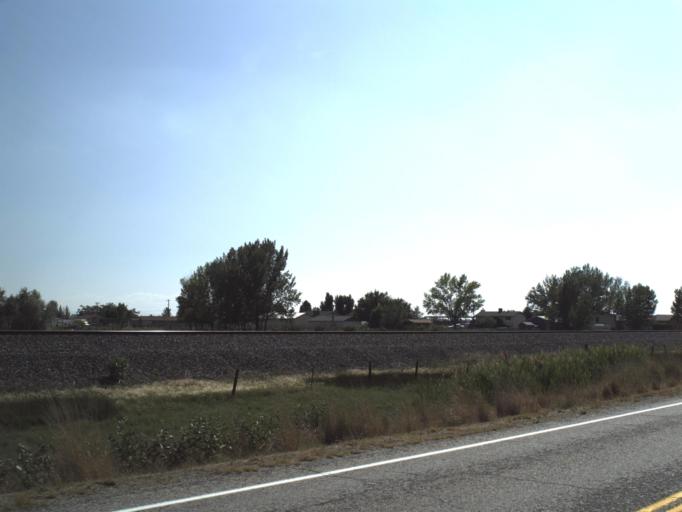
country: US
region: Utah
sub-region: Weber County
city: Marriott-Slaterville
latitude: 41.2443
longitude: -112.0572
